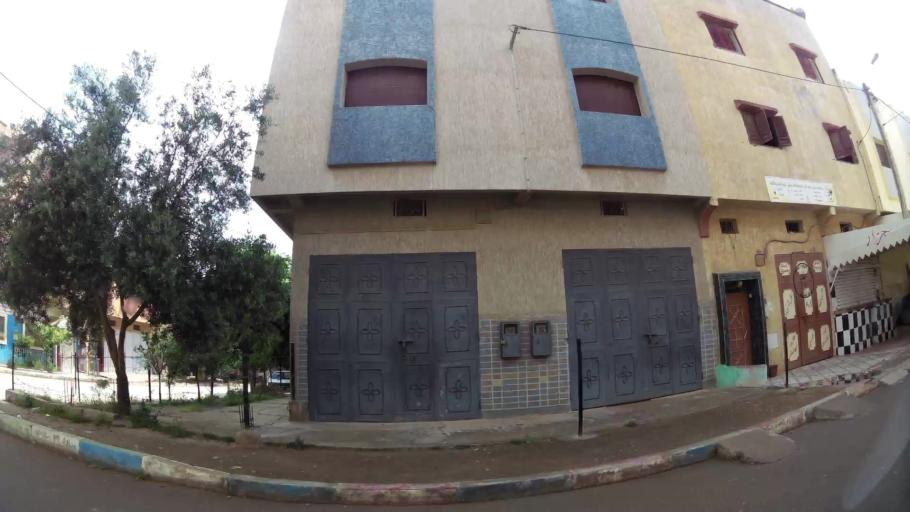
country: MA
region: Rabat-Sale-Zemmour-Zaer
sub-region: Khemisset
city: Tiflet
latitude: 33.8984
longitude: -6.3254
